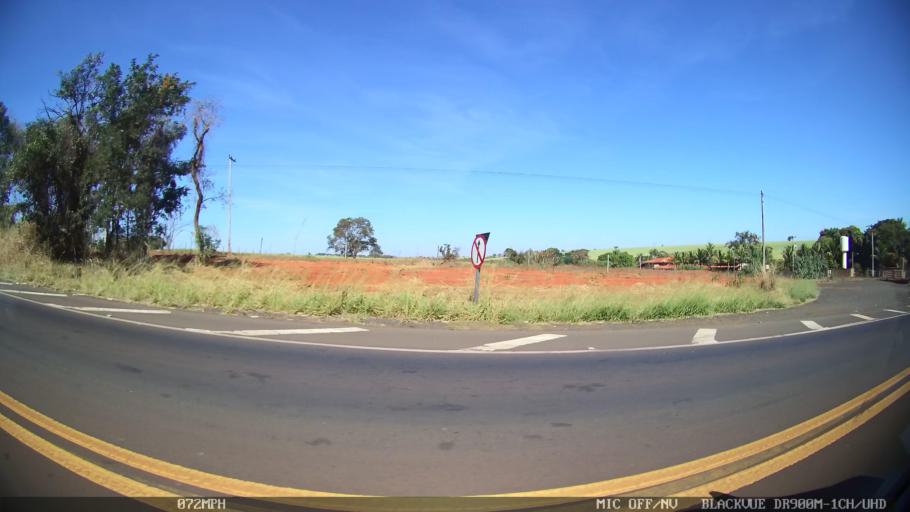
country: BR
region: Sao Paulo
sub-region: Barretos
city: Barretos
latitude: -20.5481
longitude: -48.6285
